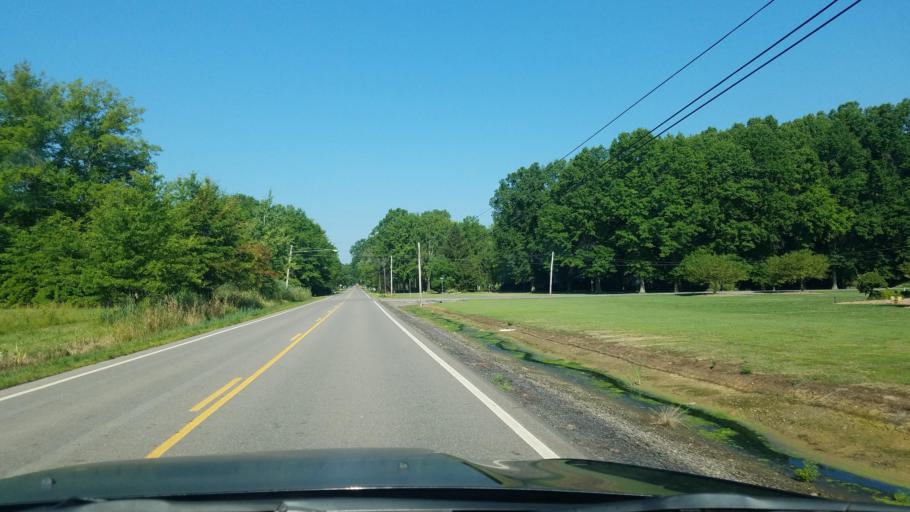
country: US
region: Ohio
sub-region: Trumbull County
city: Champion Heights
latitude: 41.3084
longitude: -80.8774
